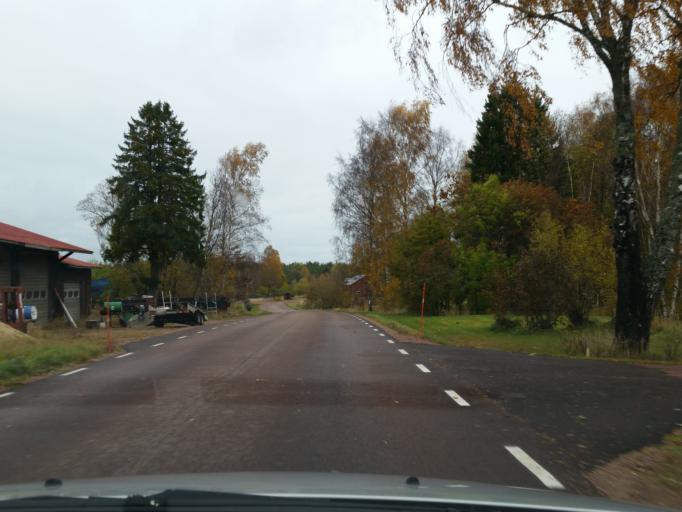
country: AX
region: Alands landsbygd
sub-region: Lemland
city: Lemland
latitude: 60.0767
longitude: 20.0832
